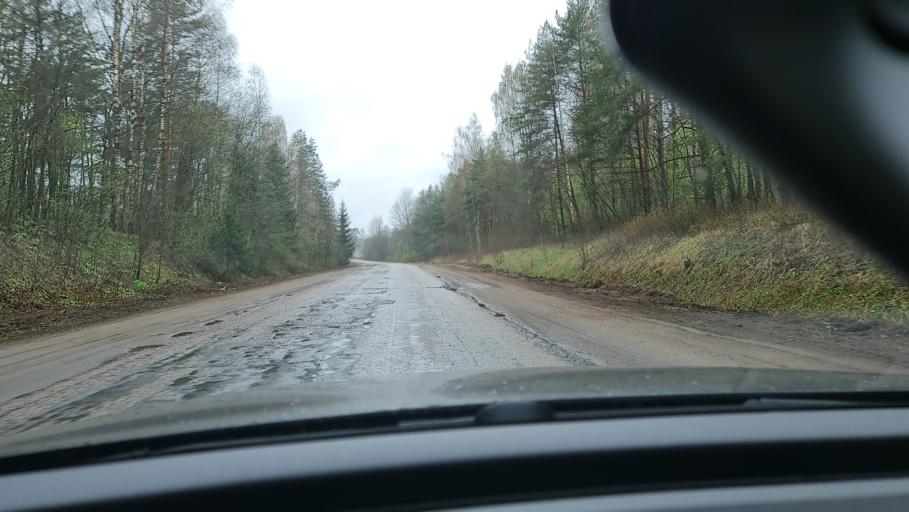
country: RU
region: Novgorod
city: Valday
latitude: 58.0409
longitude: 32.9150
